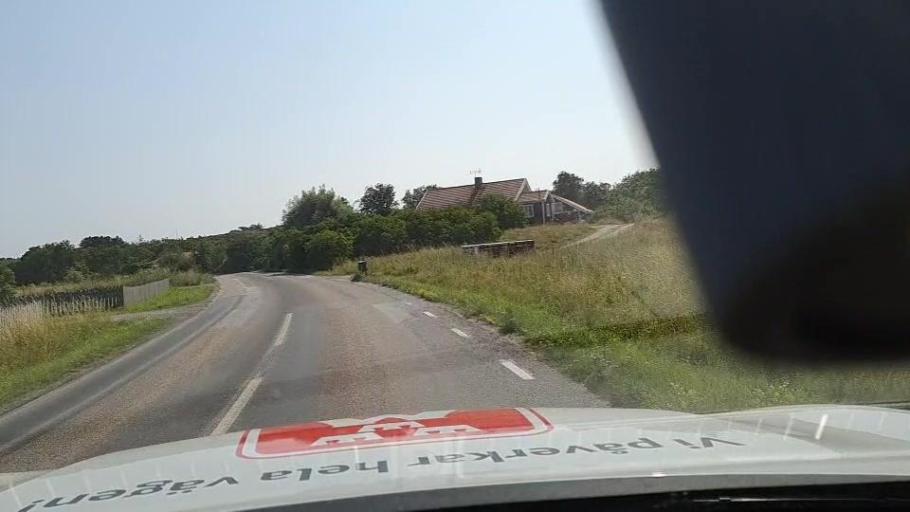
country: SE
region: Vaestra Goetaland
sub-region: Tjorns Kommun
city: Skaerhamn
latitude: 58.0873
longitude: 11.4868
